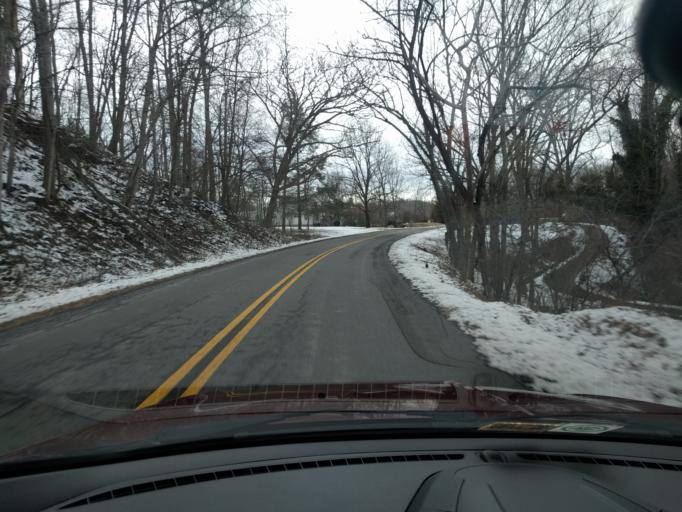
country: US
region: Virginia
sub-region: Alleghany County
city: Clifton Forge
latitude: 37.8345
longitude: -79.7448
